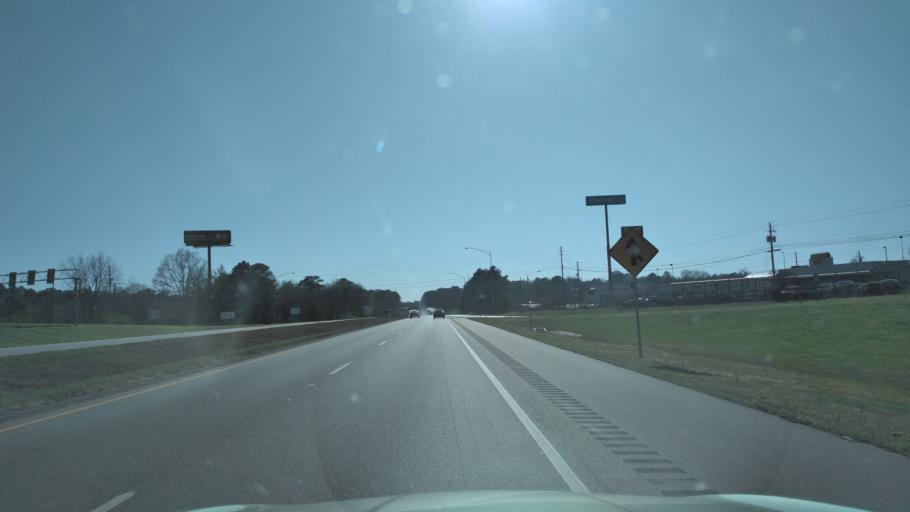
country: US
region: Alabama
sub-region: Butler County
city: Greenville
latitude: 31.8505
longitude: -86.6414
